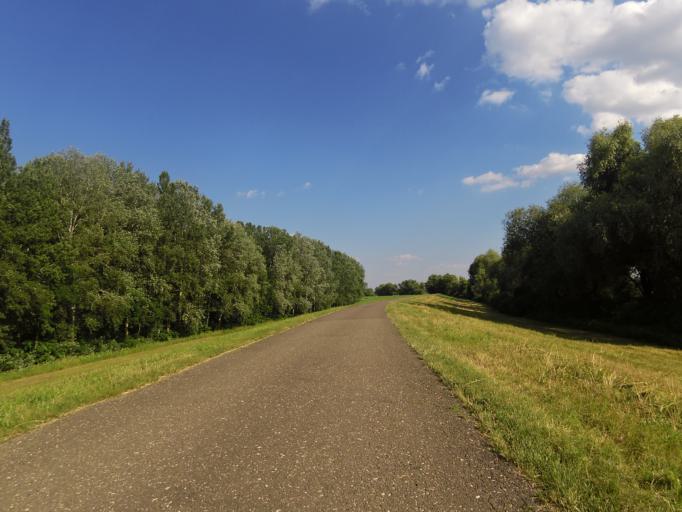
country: HU
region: Jasz-Nagykun-Szolnok
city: Abadszalok
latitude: 47.5055
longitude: 20.5964
